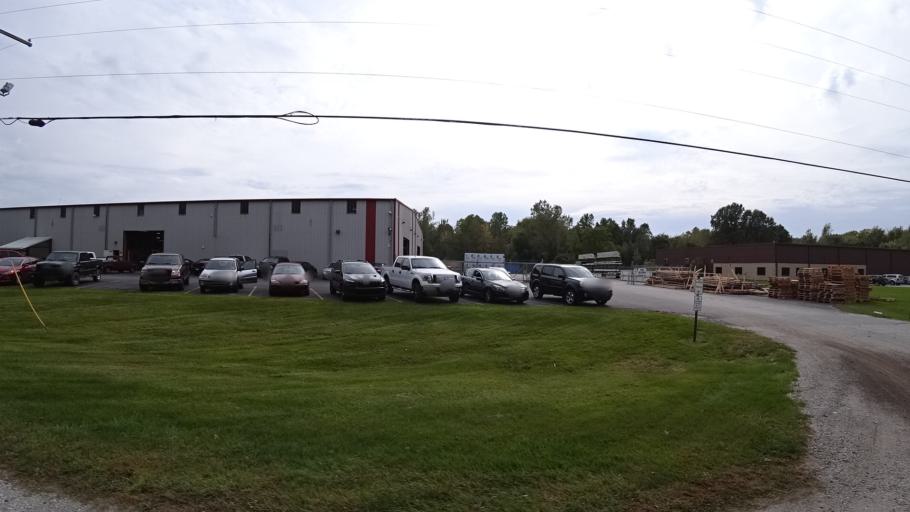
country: US
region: Indiana
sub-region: LaPorte County
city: Long Beach
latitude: 41.7237
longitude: -86.8286
